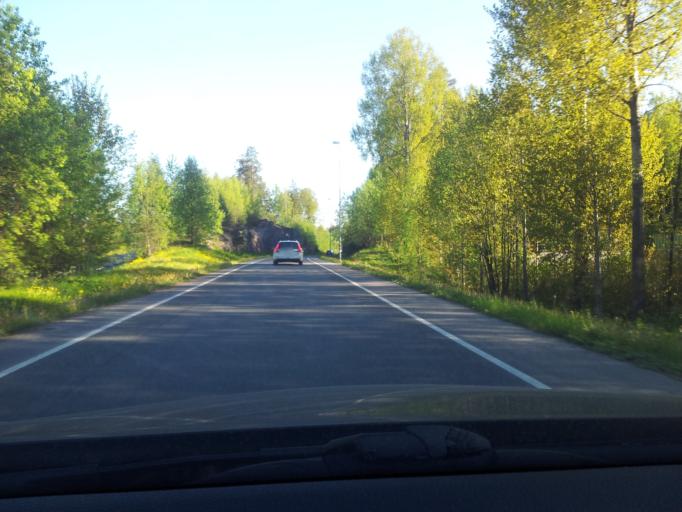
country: FI
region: Uusimaa
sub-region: Helsinki
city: Kauniainen
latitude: 60.2082
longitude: 24.7451
